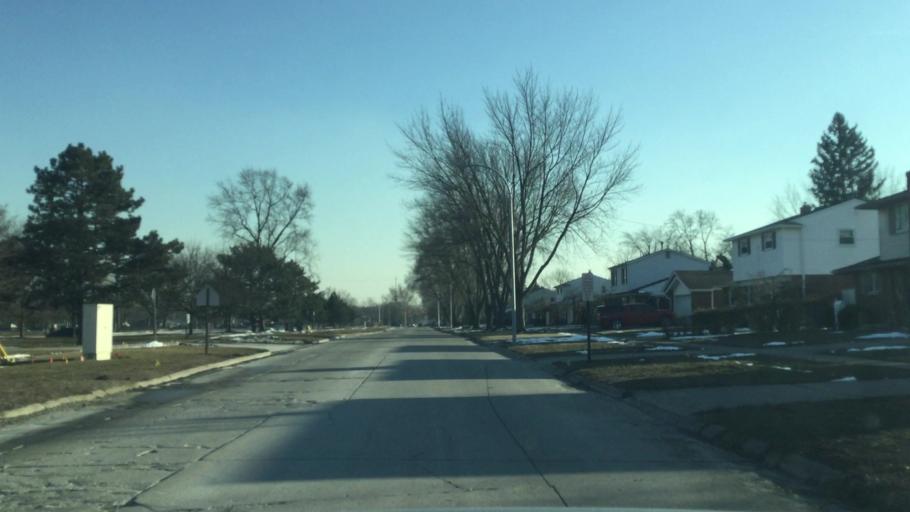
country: US
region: Michigan
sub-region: Wayne County
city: Westland
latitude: 42.3134
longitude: -83.3791
